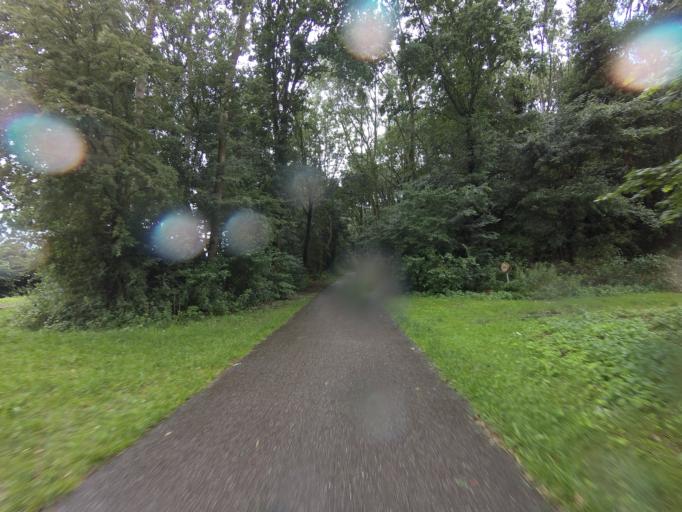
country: NL
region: Utrecht
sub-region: Gemeente Utrecht
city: Utrecht
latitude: 52.1388
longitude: 5.1010
